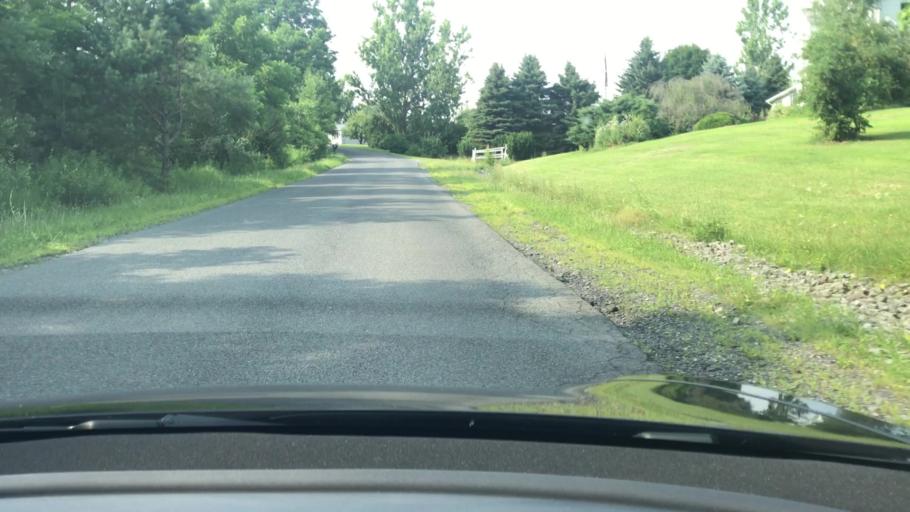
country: US
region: Pennsylvania
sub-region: Centre County
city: Stormstown
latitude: 40.7854
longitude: -78.0173
